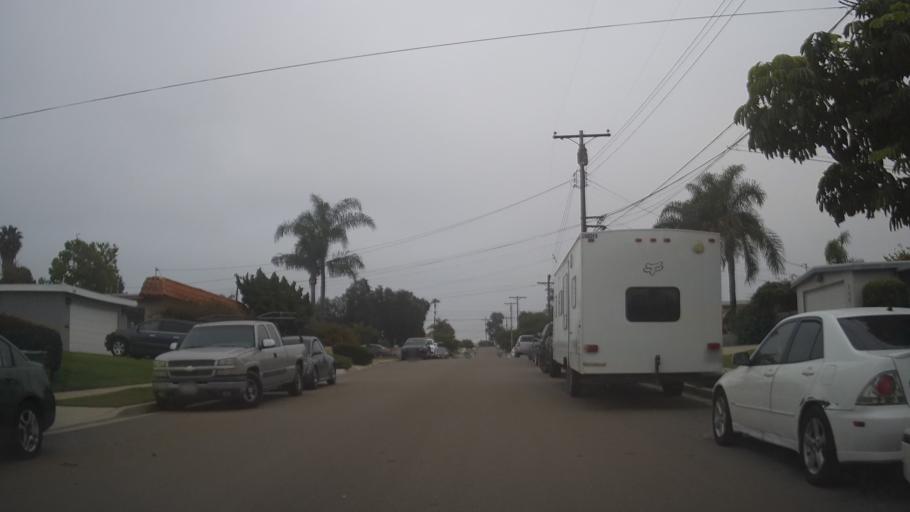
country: US
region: California
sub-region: San Diego County
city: Bonita
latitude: 32.6222
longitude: -117.0447
